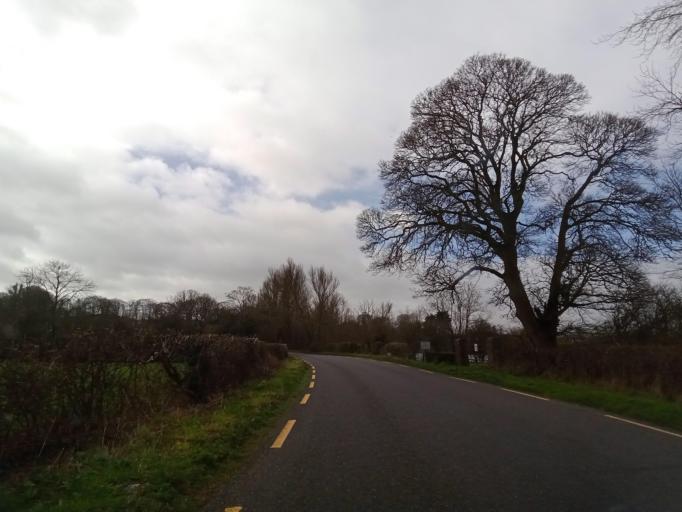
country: IE
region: Leinster
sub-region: Kilkenny
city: Ballyragget
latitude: 52.7157
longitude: -7.3212
